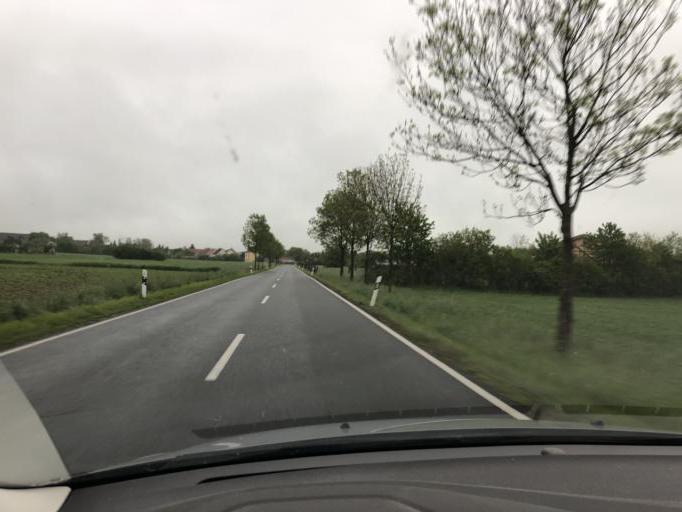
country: DE
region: Saxony
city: Taucha
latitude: 51.4356
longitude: 12.5045
